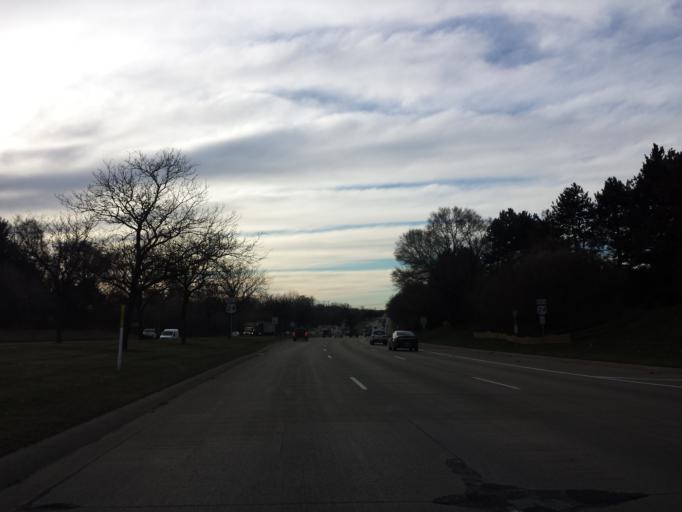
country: US
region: Michigan
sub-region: Oakland County
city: Bloomfield Hills
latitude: 42.5956
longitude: -83.2820
